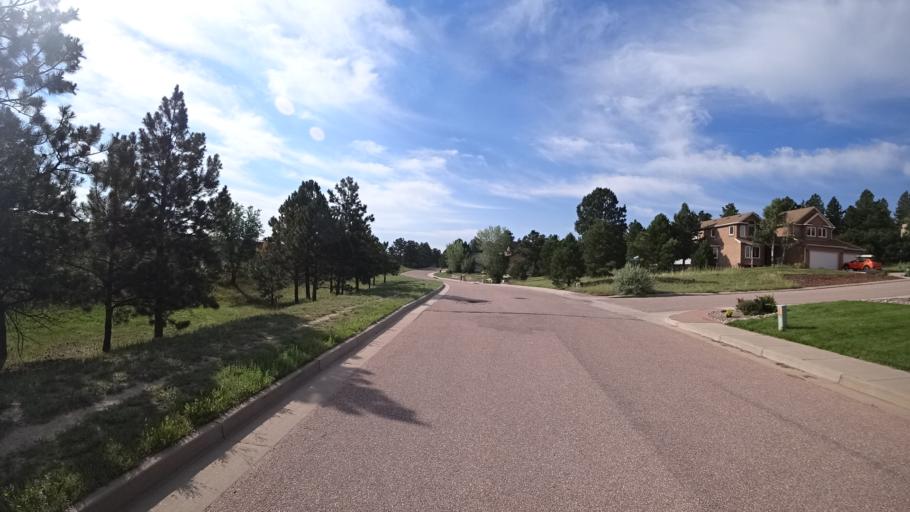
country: US
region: Colorado
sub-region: El Paso County
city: Air Force Academy
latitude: 38.9430
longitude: -104.8252
